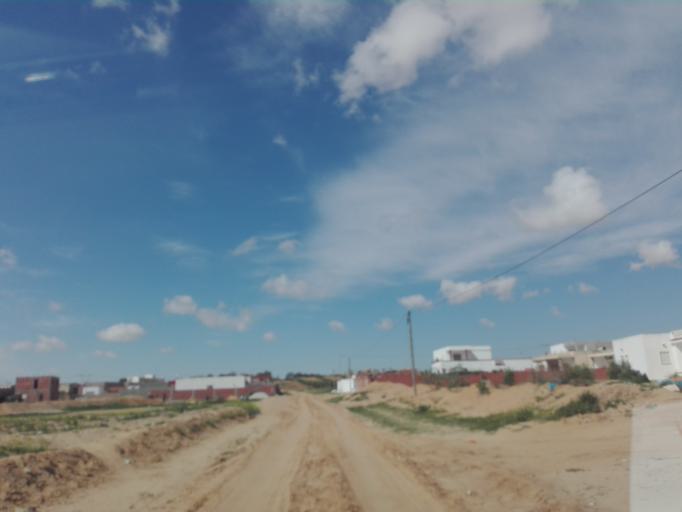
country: TN
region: Safaqis
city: Sfax
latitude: 34.7317
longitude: 10.5071
